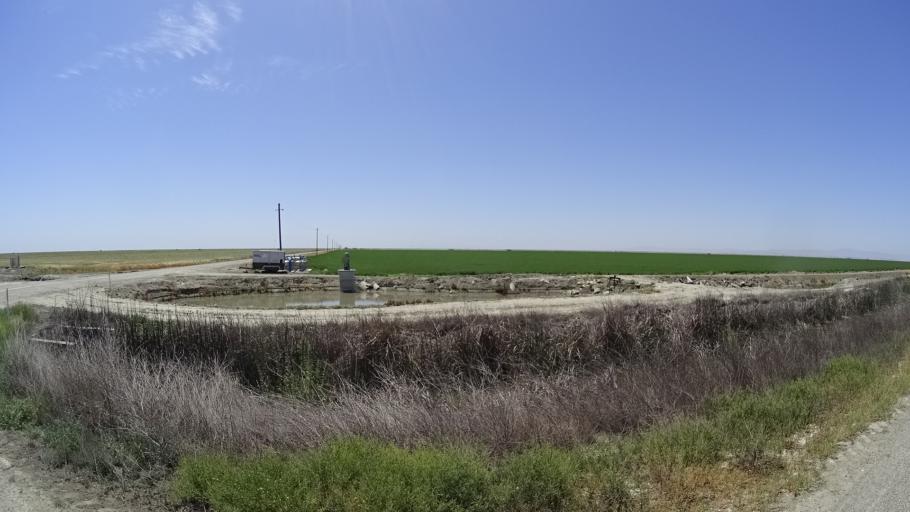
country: US
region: California
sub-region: Kings County
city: Stratford
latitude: 36.1380
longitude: -119.7342
